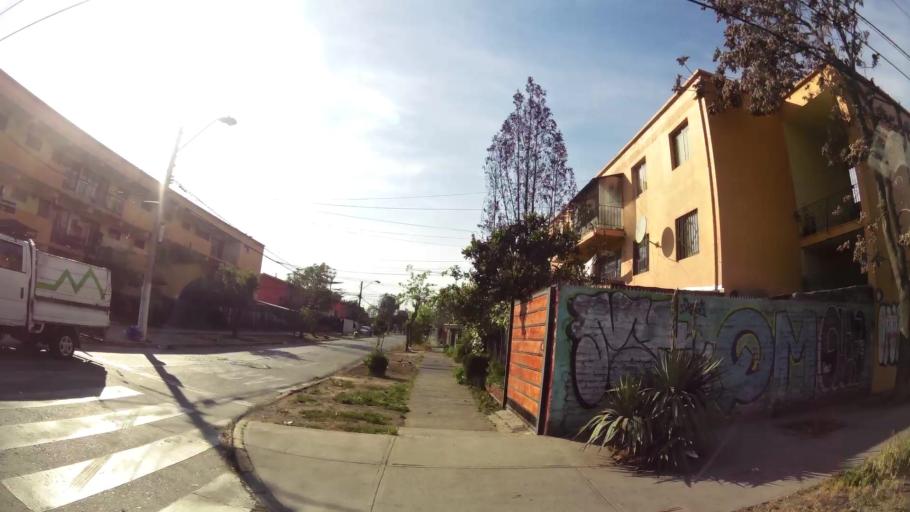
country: CL
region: Santiago Metropolitan
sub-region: Provincia de Santiago
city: Santiago
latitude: -33.5013
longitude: -70.6663
